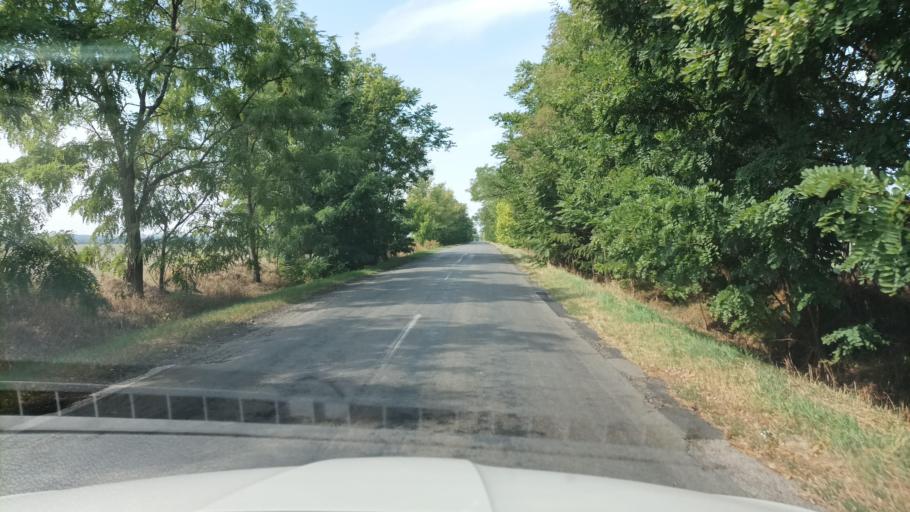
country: HU
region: Heves
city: Boldog
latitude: 47.6143
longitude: 19.6497
